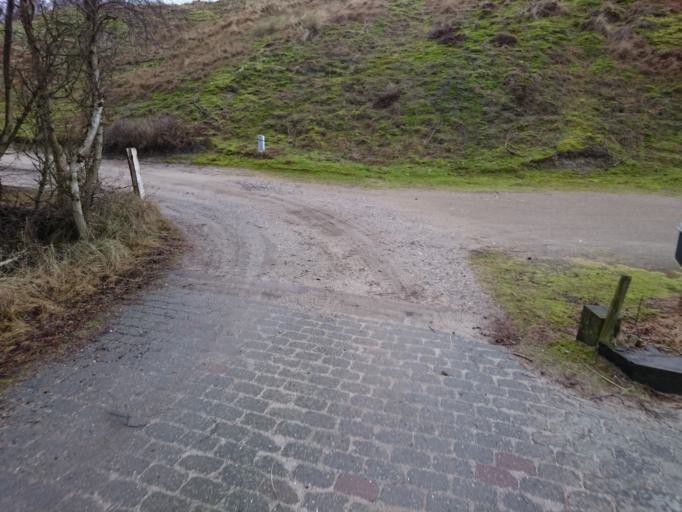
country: DK
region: South Denmark
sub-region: Fano Kommune
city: Nordby
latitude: 55.4370
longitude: 8.3791
